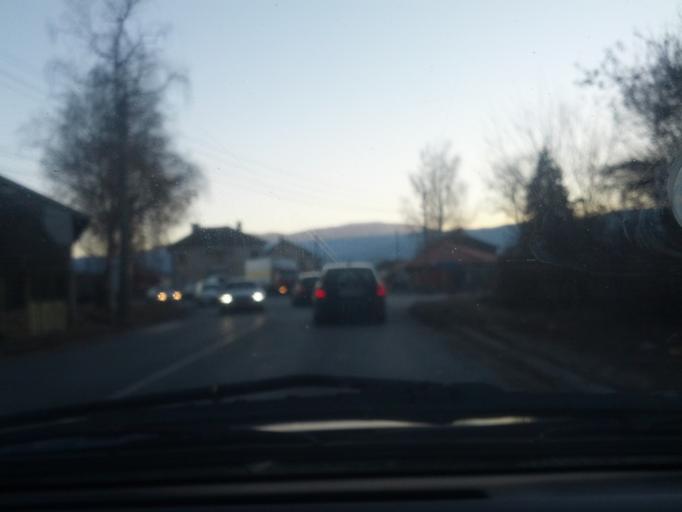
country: BG
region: Sofiya
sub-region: Obshtina Botevgrad
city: Botevgrad
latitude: 42.9810
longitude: 23.7331
